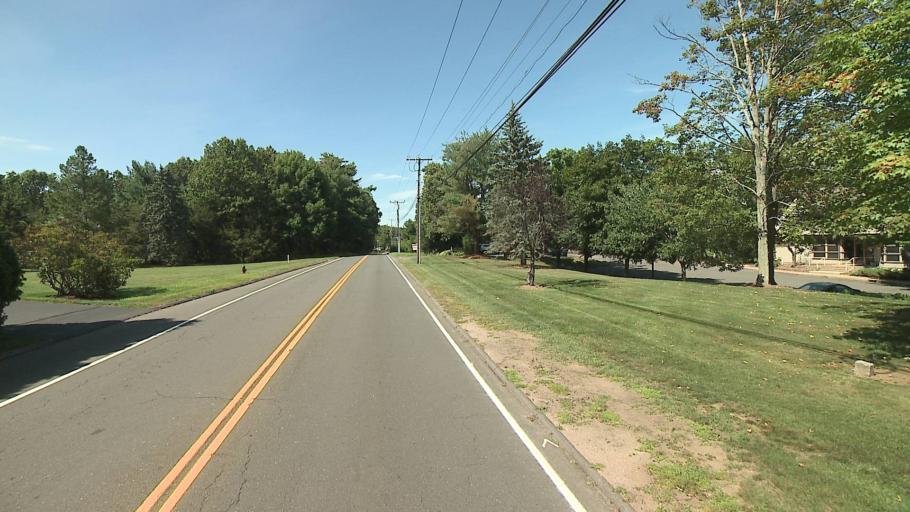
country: US
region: Connecticut
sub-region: Hartford County
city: Canton Valley
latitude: 41.8130
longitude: -72.8663
